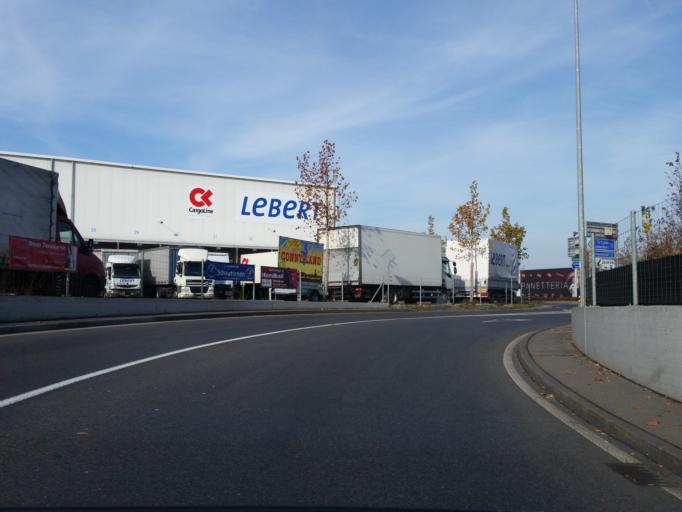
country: DE
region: Baden-Wuerttemberg
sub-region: Freiburg Region
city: Konstanz
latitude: 47.6542
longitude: 9.1646
